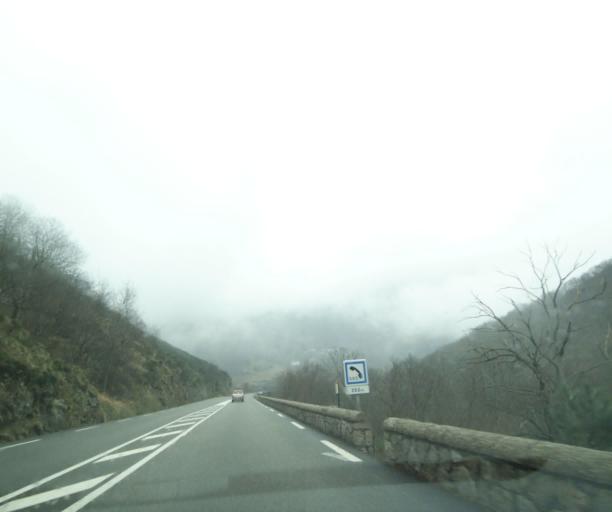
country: FR
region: Rhone-Alpes
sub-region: Departement de l'Ardeche
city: Thueyts
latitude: 44.6733
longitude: 4.0967
